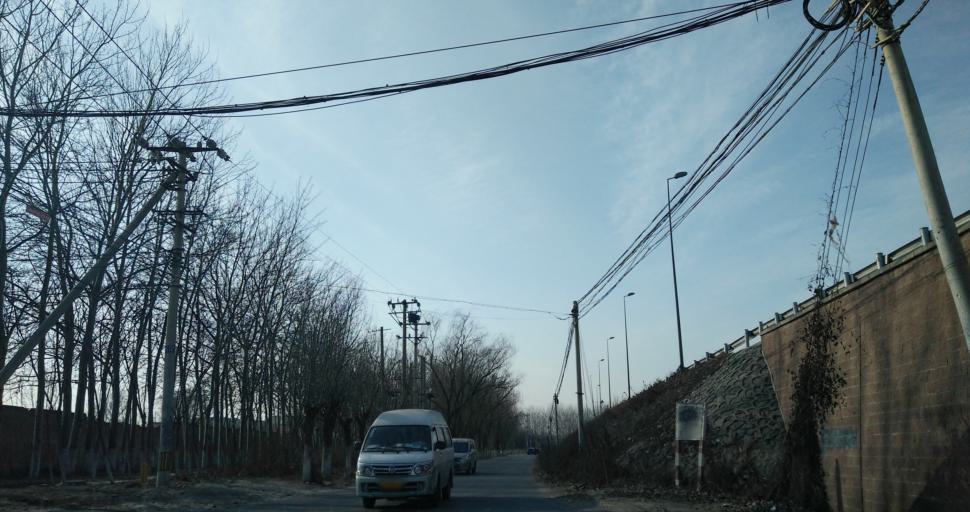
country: CN
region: Beijing
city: Xingfeng
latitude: 39.7193
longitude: 116.3902
